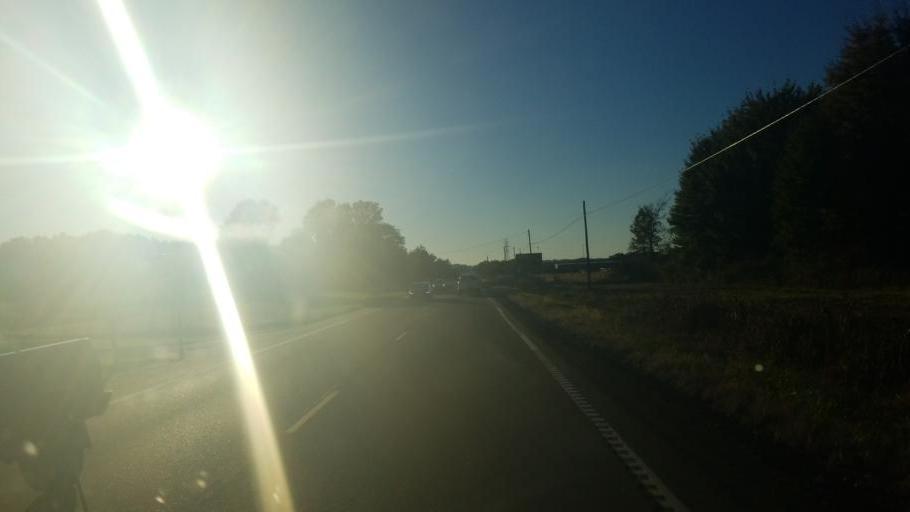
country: US
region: Ohio
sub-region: Mahoning County
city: Sebring
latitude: 40.9015
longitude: -81.0401
